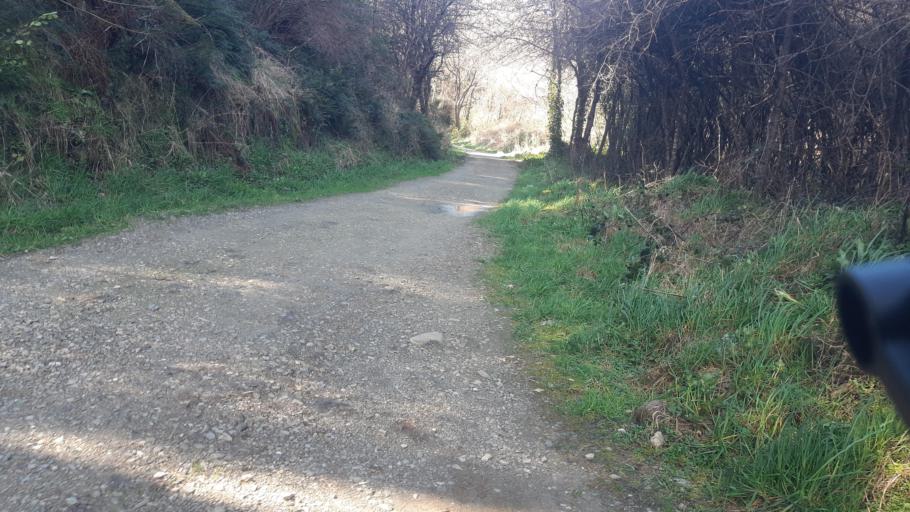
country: NZ
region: Tasman
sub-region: Tasman District
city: Wakefield
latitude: -41.4891
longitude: 172.8947
